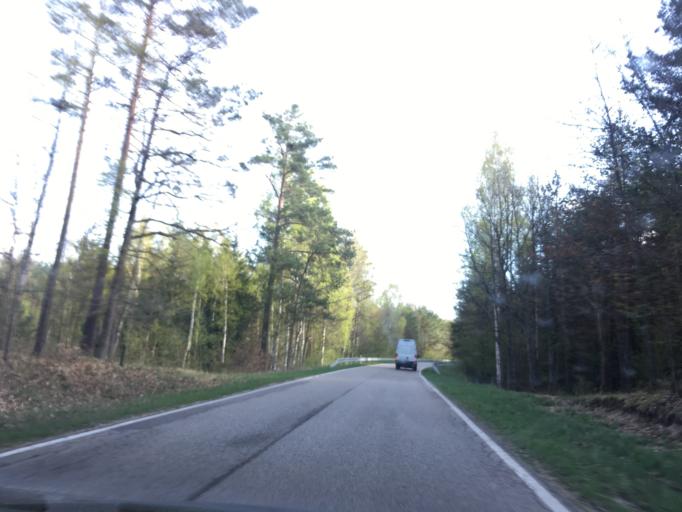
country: PL
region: Warmian-Masurian Voivodeship
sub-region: Powiat piski
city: Ruciane-Nida
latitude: 53.6716
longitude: 21.5771
